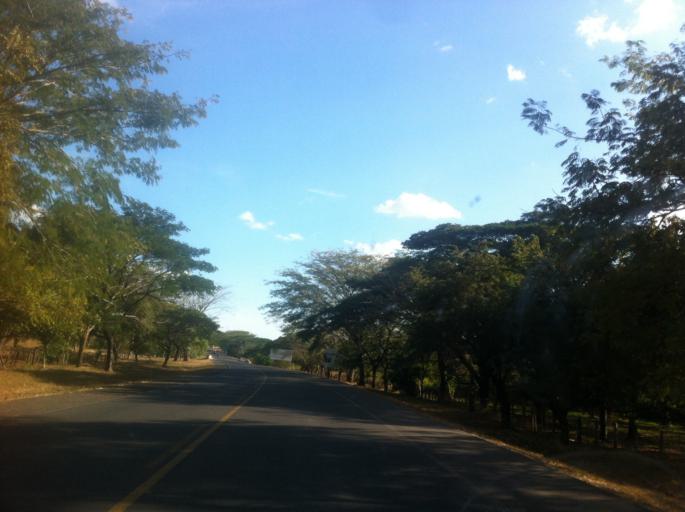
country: NI
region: Chontales
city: Acoyapa
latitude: 11.9774
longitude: -85.1690
